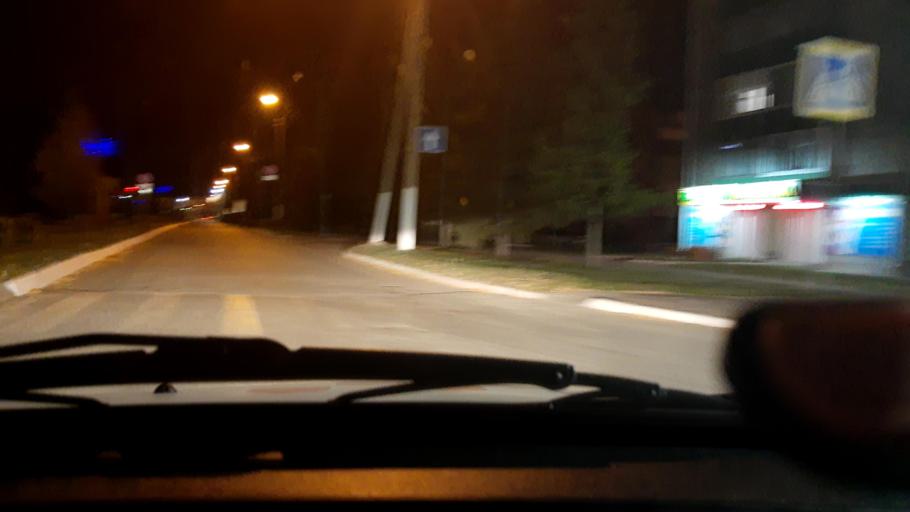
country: RU
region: Bashkortostan
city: Belebey
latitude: 54.0999
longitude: 54.1061
